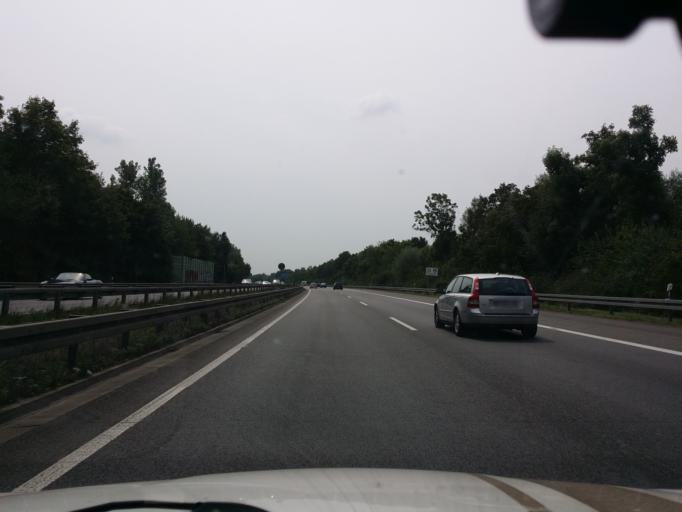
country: DE
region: Hesse
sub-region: Regierungsbezirk Darmstadt
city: Bensheim
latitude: 49.6787
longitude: 8.5993
